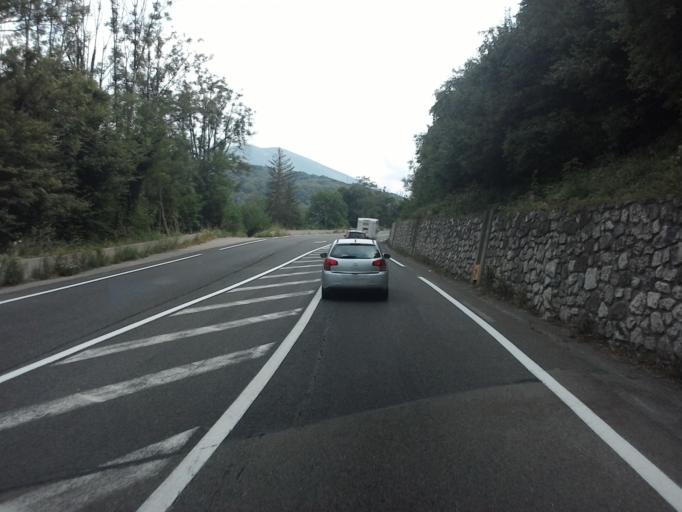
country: FR
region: Rhone-Alpes
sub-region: Departement de l'Isere
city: Notre-Dame-de-Mesage
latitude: 45.0408
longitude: 5.7643
